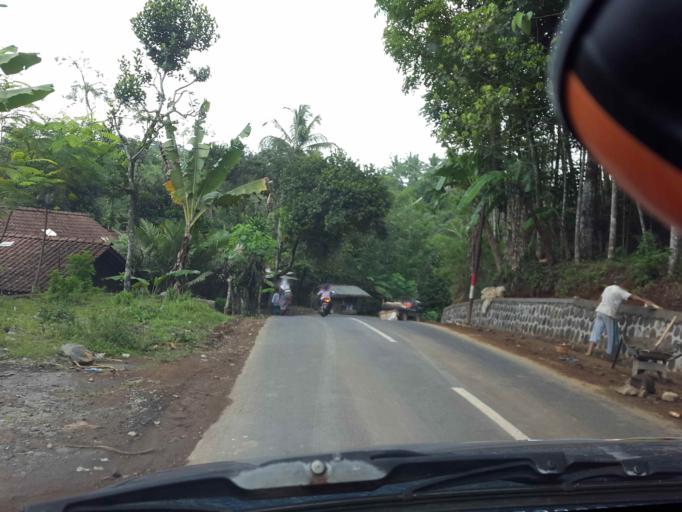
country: ID
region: Central Java
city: Magelang
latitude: -7.5172
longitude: 110.0485
